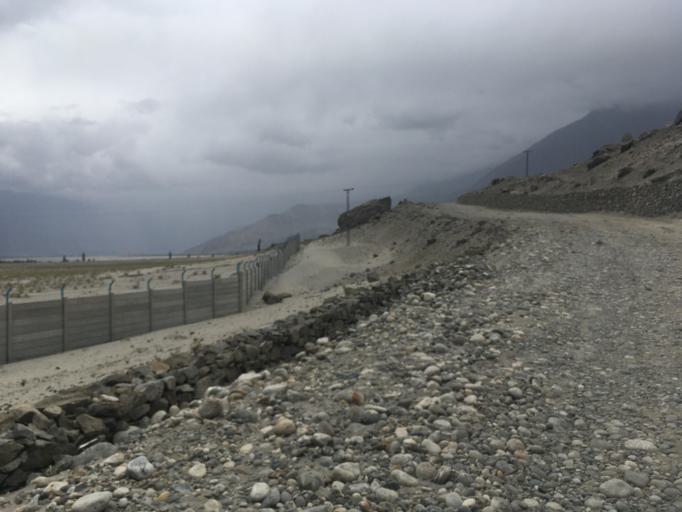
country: PK
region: Gilgit-Baltistan
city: Skardu
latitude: 35.3178
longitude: 75.6570
